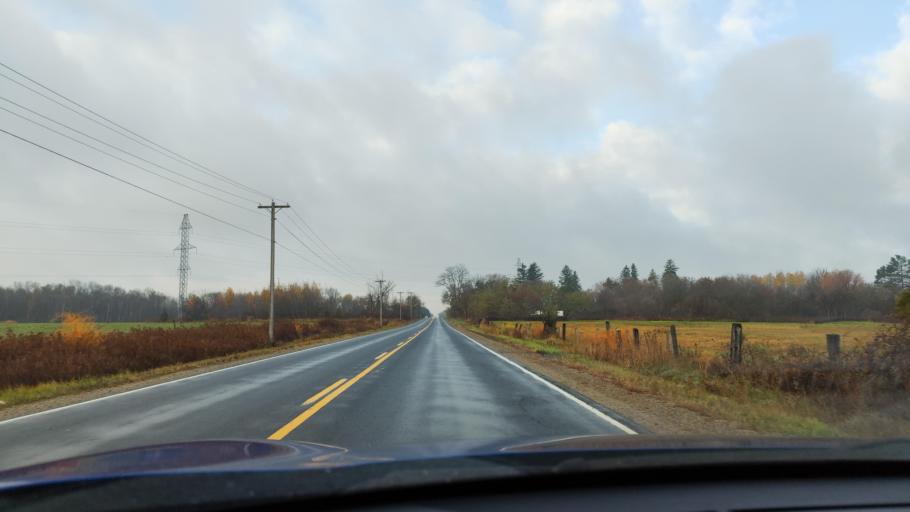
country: CA
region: Ontario
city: Angus
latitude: 44.3638
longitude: -79.9473
